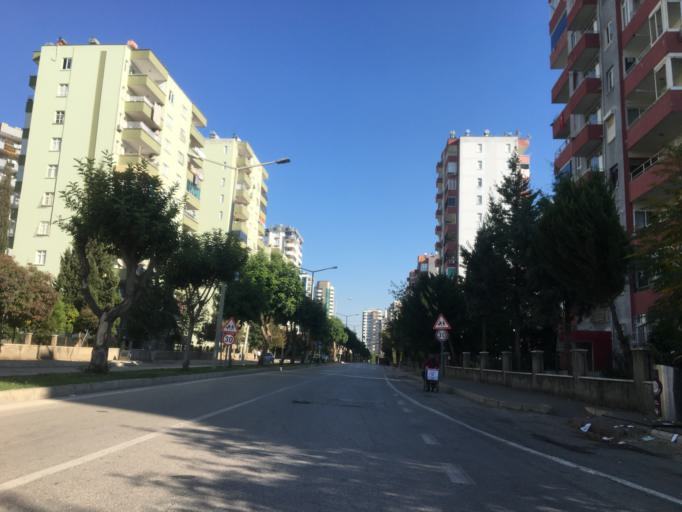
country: TR
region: Adana
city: Seyhan
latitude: 37.0282
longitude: 35.2553
